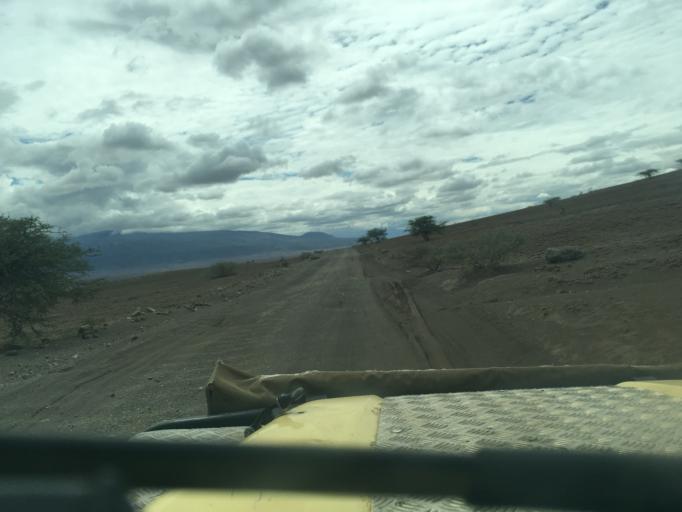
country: TZ
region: Arusha
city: Mto wa Mbu
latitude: -2.8218
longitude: 36.0093
